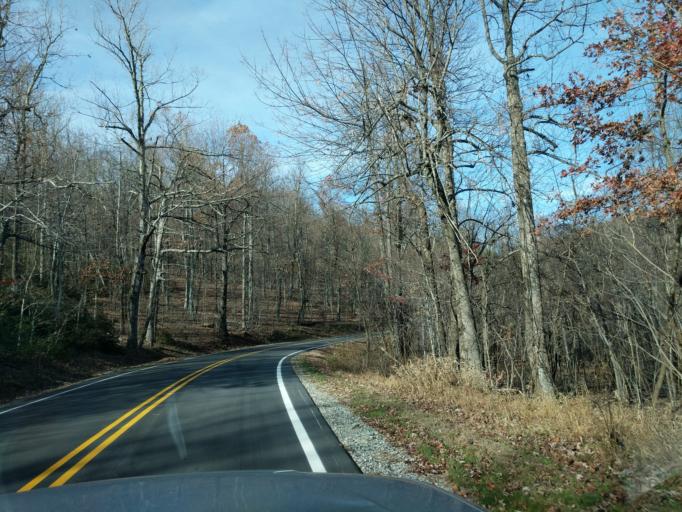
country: US
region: North Carolina
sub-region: Polk County
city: Columbus
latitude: 35.2765
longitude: -82.2194
